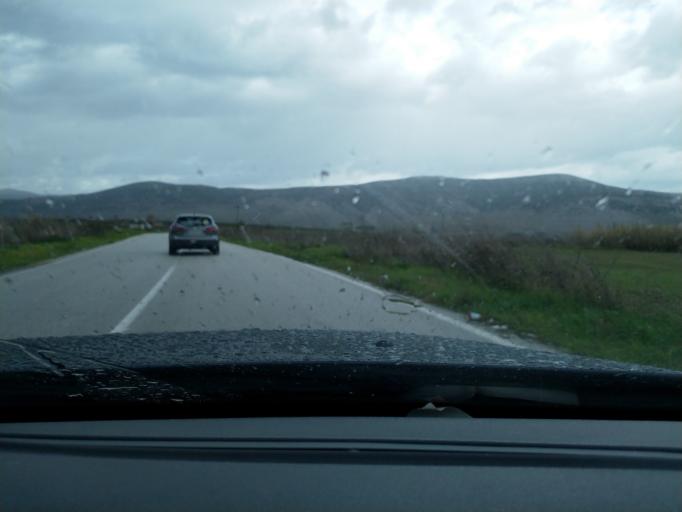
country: GR
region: Thessaly
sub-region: Trikala
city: Taxiarches
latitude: 39.5546
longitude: 21.8901
